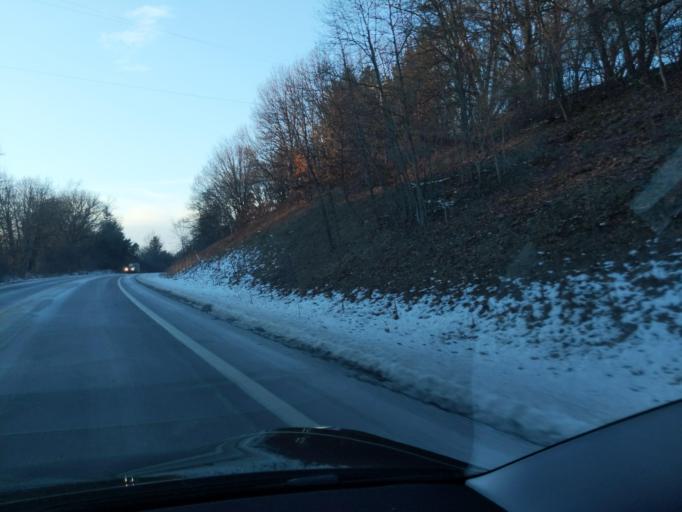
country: US
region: Michigan
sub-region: Ingham County
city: Mason
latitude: 42.5562
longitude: -84.3688
